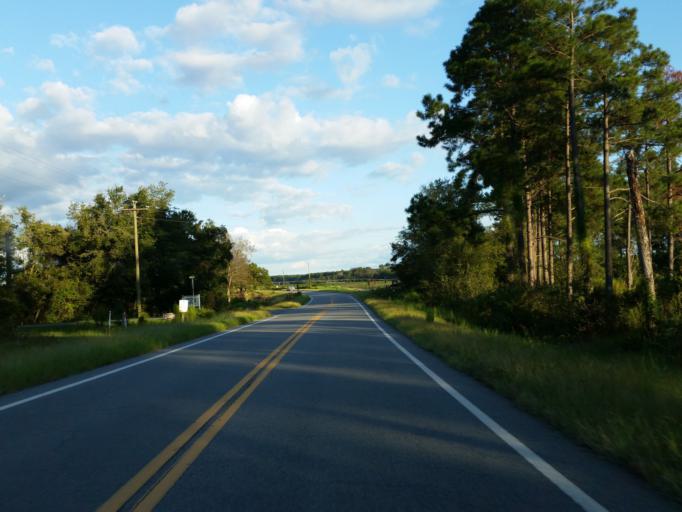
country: US
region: Georgia
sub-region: Dooly County
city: Vienna
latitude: 32.0854
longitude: -83.7146
